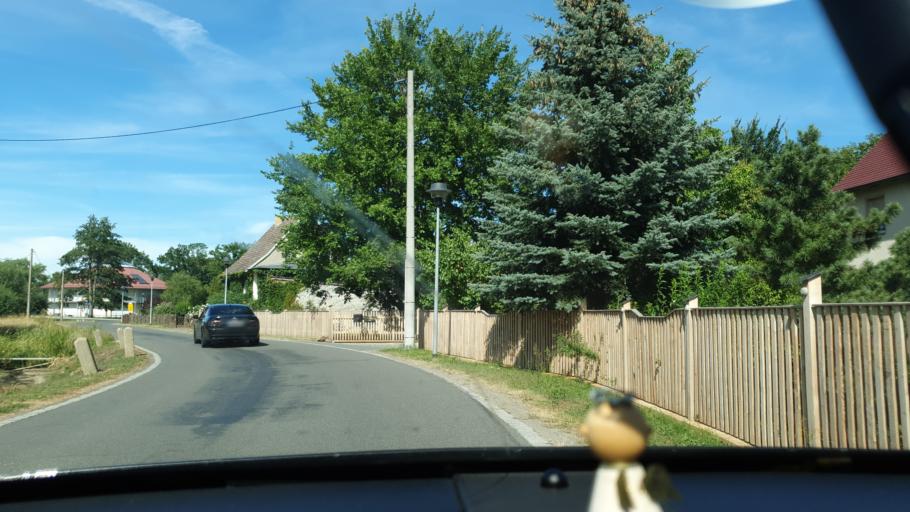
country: DE
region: Saxony
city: Mockrehna
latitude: 51.4994
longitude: 12.8430
